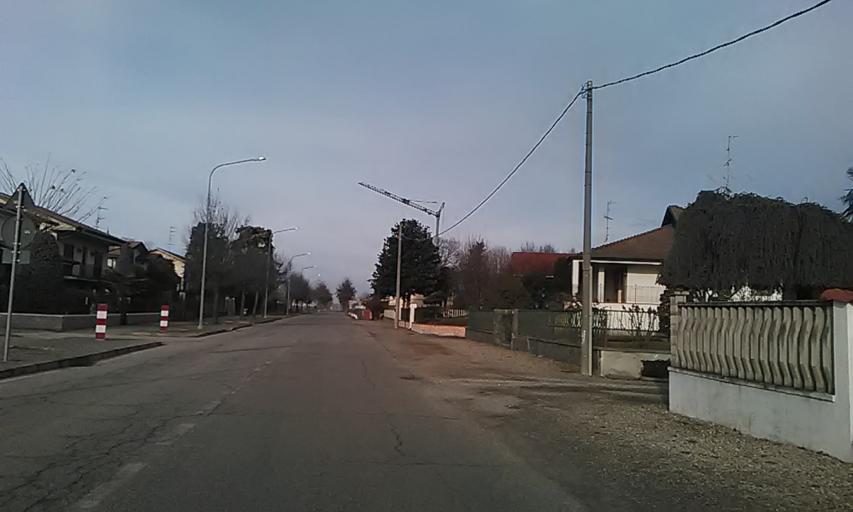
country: IT
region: Piedmont
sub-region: Provincia di Vercelli
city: Stroppiana
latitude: 45.2349
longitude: 8.4559
